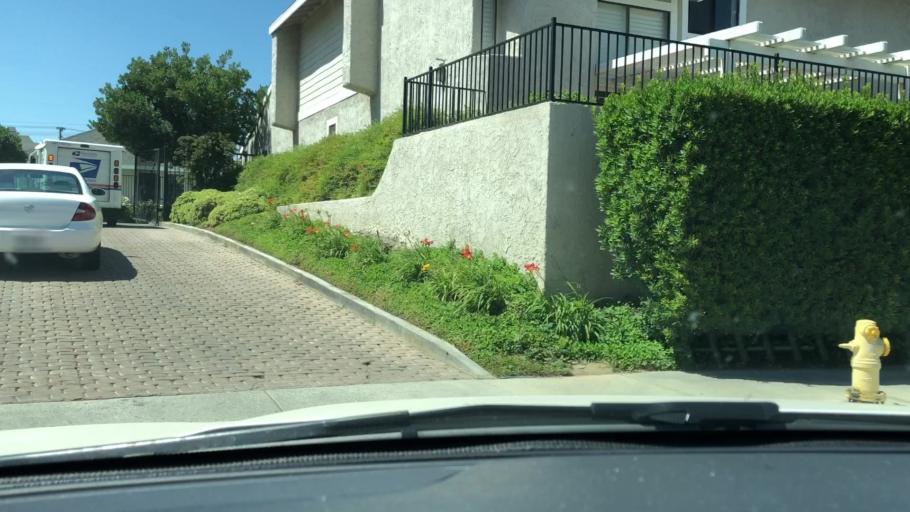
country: US
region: California
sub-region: Los Angeles County
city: Santa Clarita
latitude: 34.3897
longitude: -118.5422
